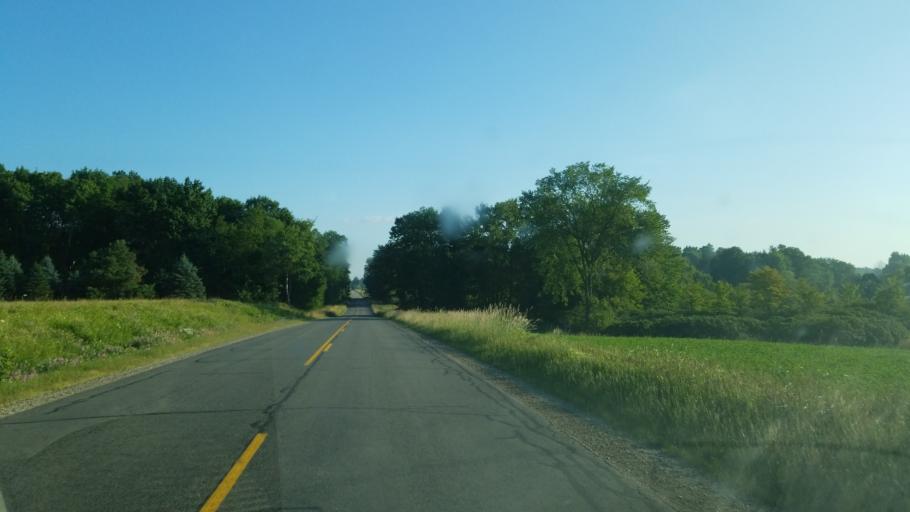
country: US
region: Michigan
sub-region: Mecosta County
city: Canadian Lakes
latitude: 43.5347
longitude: -85.1846
